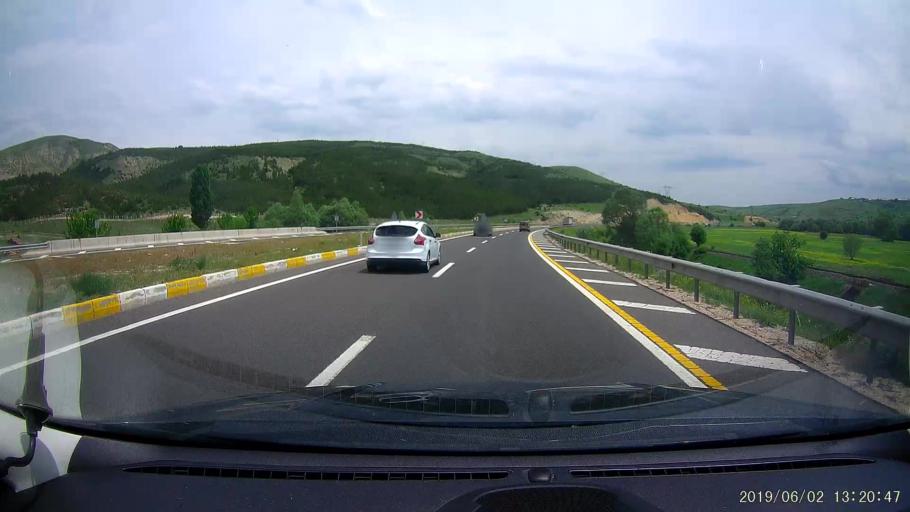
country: TR
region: Cankiri
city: Cerkes
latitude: 40.8421
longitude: 32.7675
